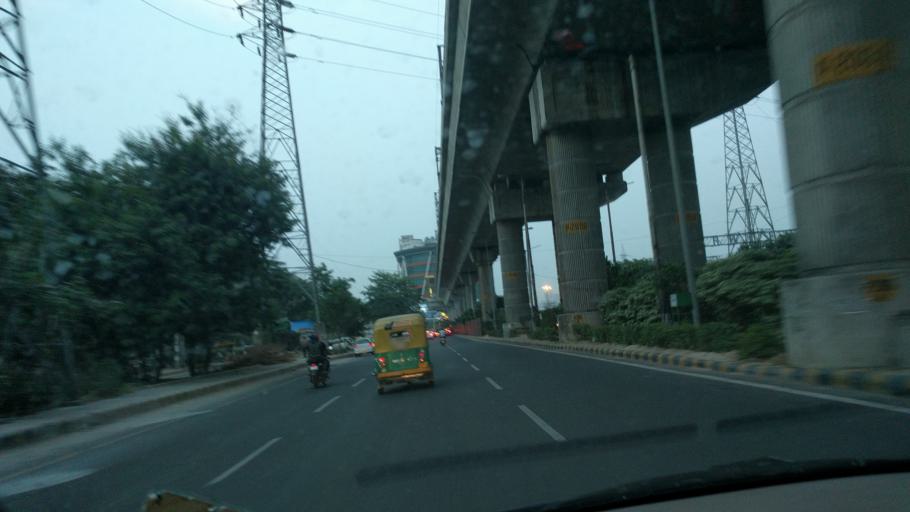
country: IN
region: Haryana
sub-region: Gurgaon
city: Gurgaon
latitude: 28.4567
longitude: 77.0703
